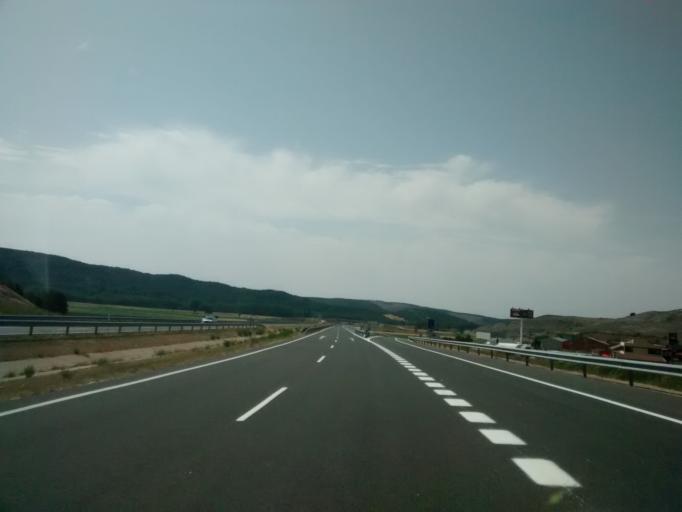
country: ES
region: Castille and Leon
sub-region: Provincia de Palencia
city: Alar del Rey
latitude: 42.7205
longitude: -4.2910
